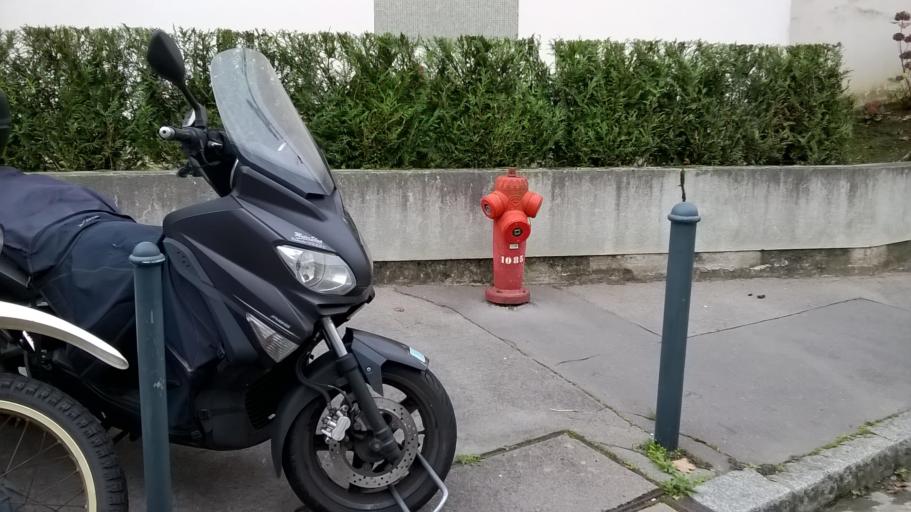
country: FR
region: Pays de la Loire
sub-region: Departement de la Loire-Atlantique
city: Nantes
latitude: 47.2281
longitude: -1.5579
